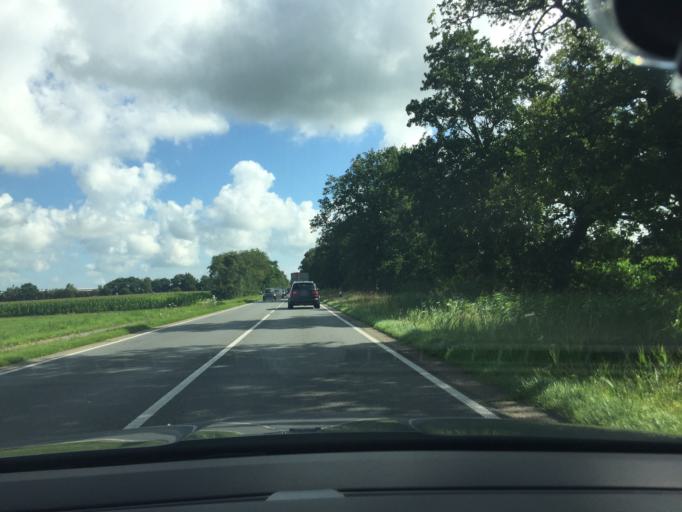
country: DE
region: Lower Saxony
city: Blomberg
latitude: 53.5338
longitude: 7.5900
